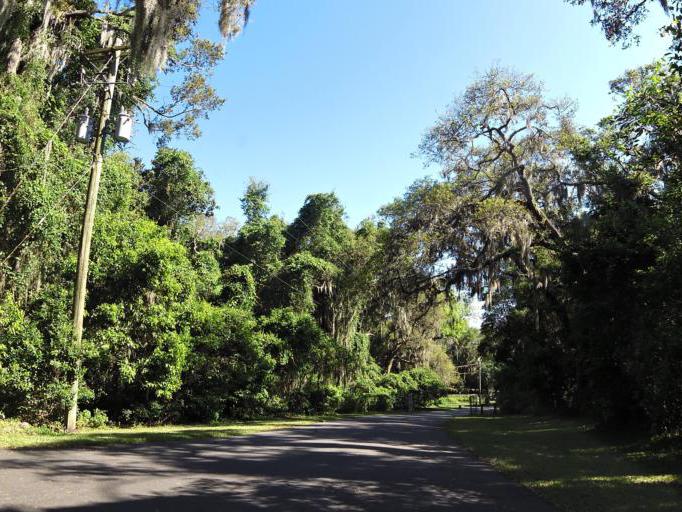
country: US
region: Florida
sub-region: Duval County
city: Atlantic Beach
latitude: 30.3877
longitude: -81.4898
